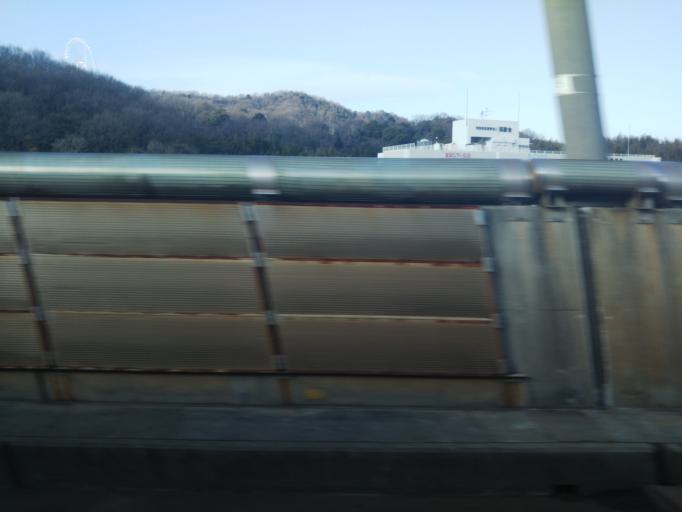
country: JP
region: Kagawa
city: Sakaidecho
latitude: 34.4509
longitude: 133.8076
